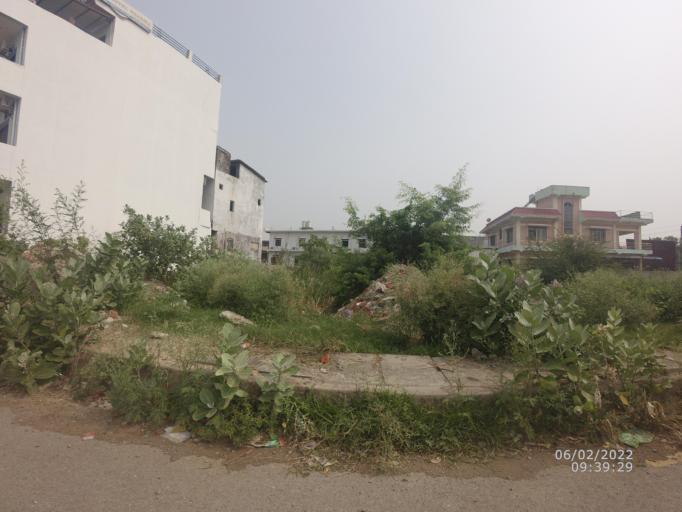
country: NP
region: Western Region
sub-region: Lumbini Zone
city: Bhairahawa
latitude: 27.4997
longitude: 83.4574
